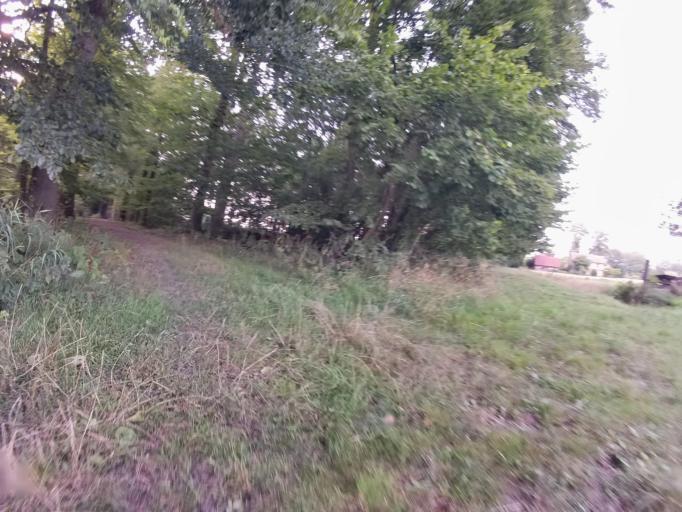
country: DE
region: North Rhine-Westphalia
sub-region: Regierungsbezirk Munster
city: Mettingen
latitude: 52.3084
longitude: 7.8246
